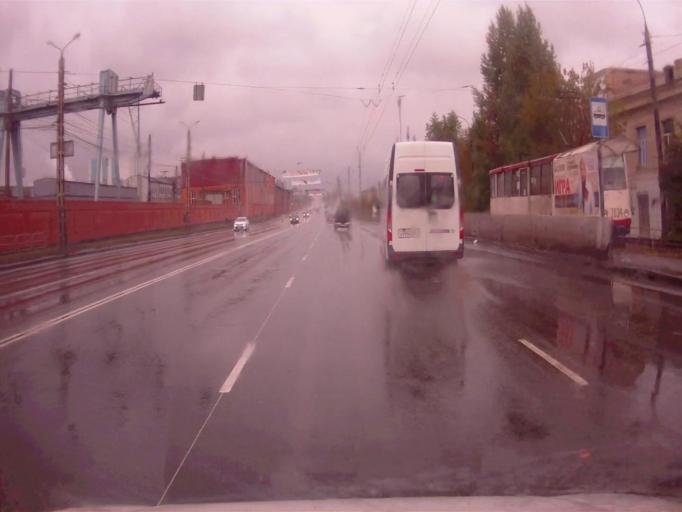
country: RU
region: Chelyabinsk
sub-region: Gorod Chelyabinsk
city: Chelyabinsk
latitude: 55.2059
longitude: 61.3848
